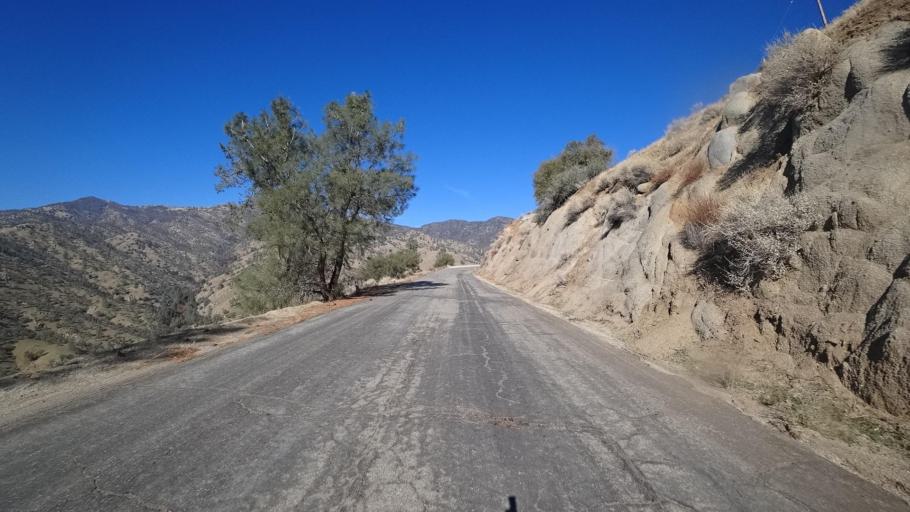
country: US
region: California
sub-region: Kern County
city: Bodfish
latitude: 35.5476
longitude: -118.6113
